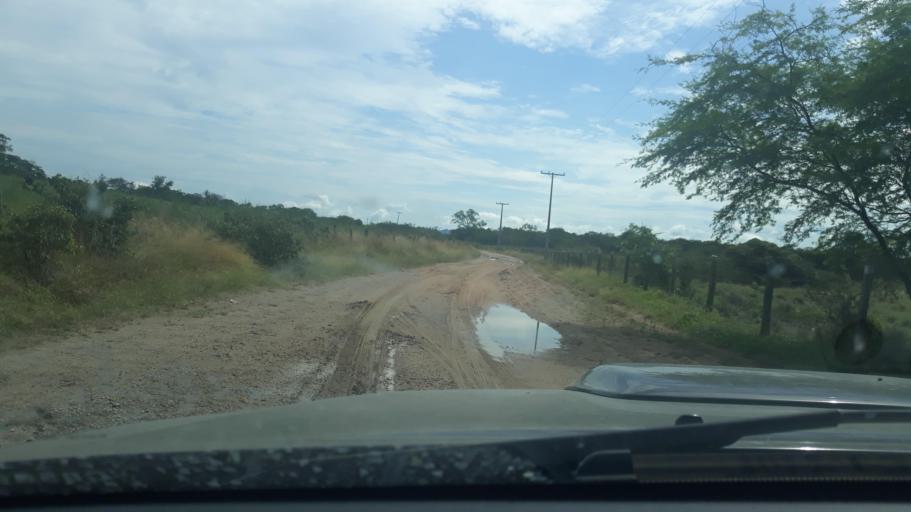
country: BR
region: Bahia
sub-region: Riacho De Santana
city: Riacho de Santana
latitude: -13.8798
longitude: -43.0209
